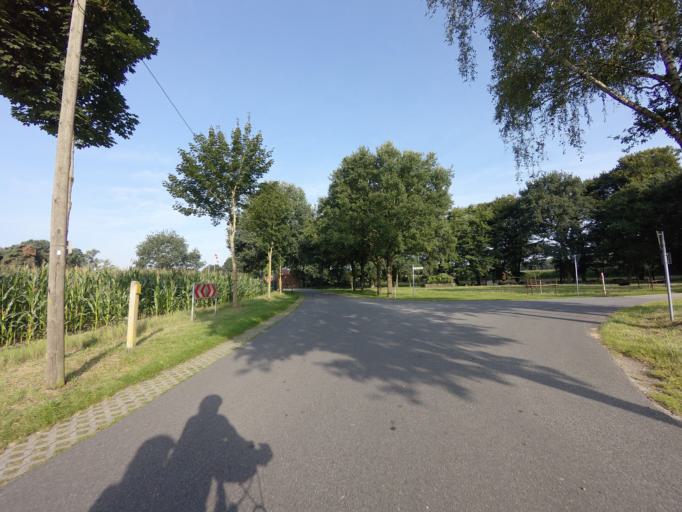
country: DE
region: Lower Saxony
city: Itterbeck
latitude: 52.4904
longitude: 6.8108
